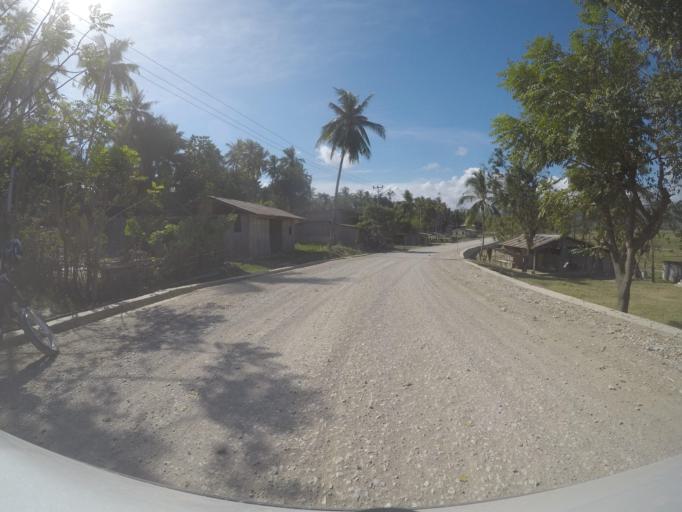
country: TL
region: Viqueque
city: Viqueque
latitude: -8.8206
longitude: 126.5328
